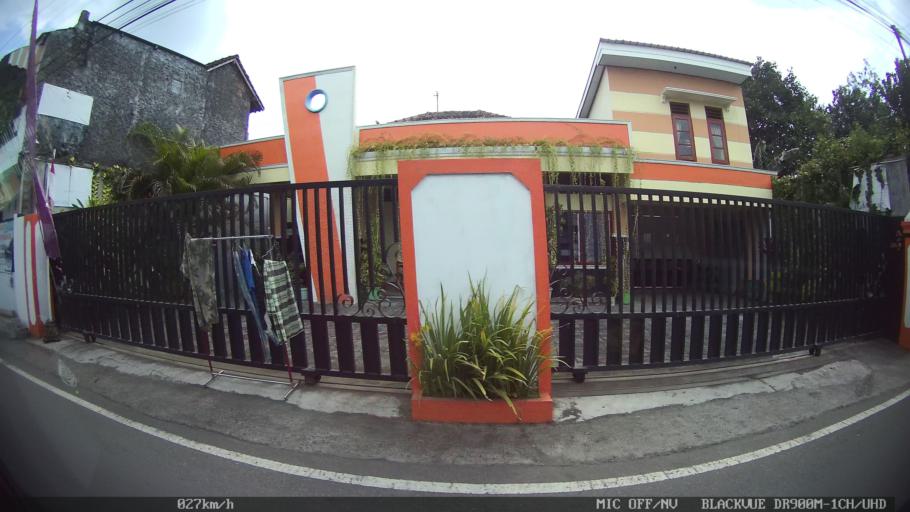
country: ID
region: Daerah Istimewa Yogyakarta
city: Gamping Lor
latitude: -7.8040
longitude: 110.3279
